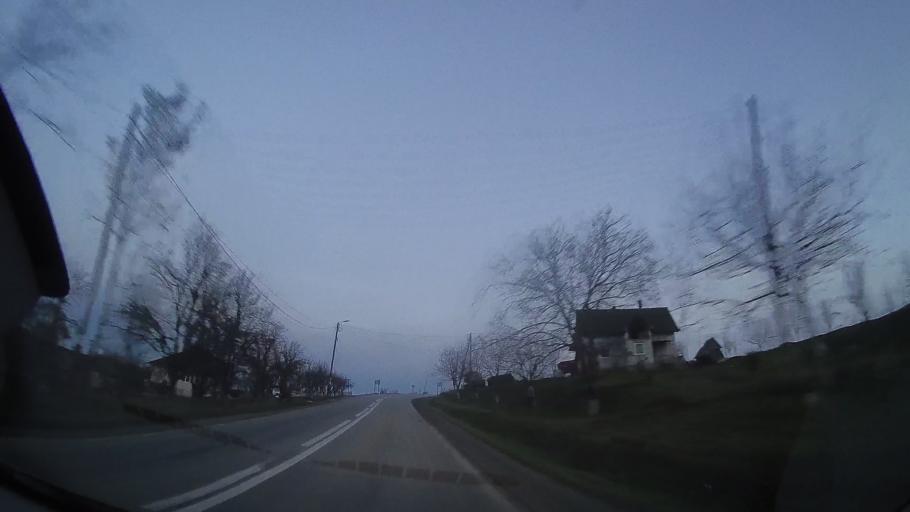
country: RO
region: Cluj
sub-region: Comuna Mociu
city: Mociu
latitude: 46.7899
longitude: 24.0773
